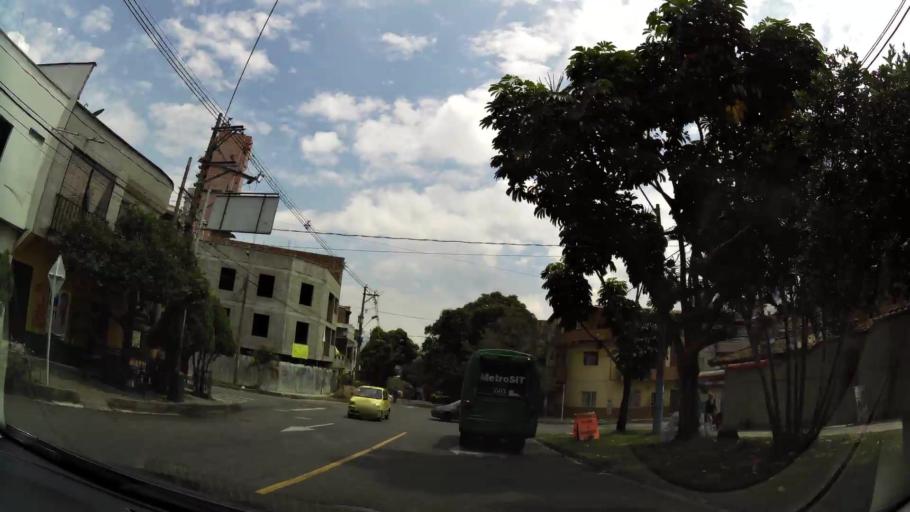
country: CO
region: Antioquia
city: Medellin
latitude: 6.2523
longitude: -75.6100
